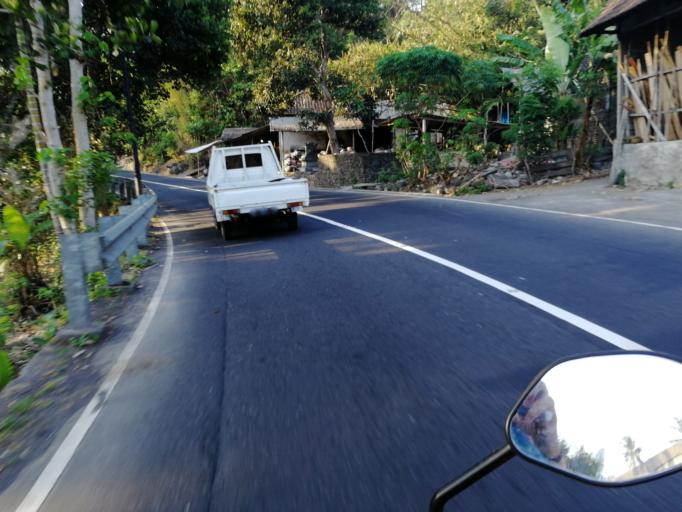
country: ID
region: Bali
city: Tistagede
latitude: -8.3761
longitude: 115.6077
